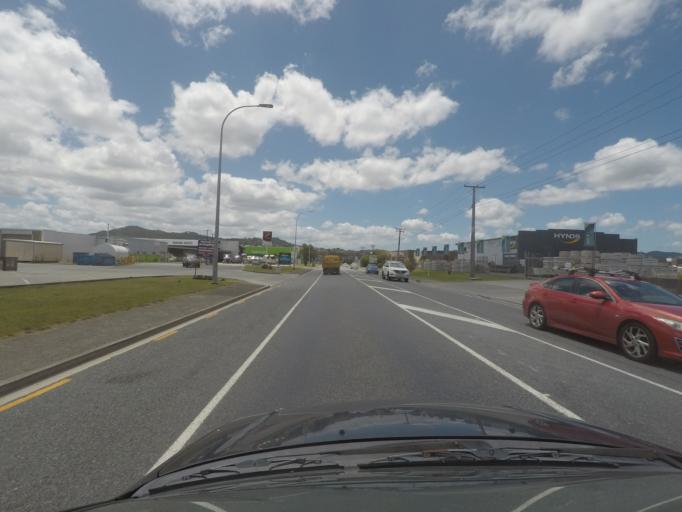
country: NZ
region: Northland
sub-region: Whangarei
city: Whangarei
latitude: -35.7422
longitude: 174.3317
